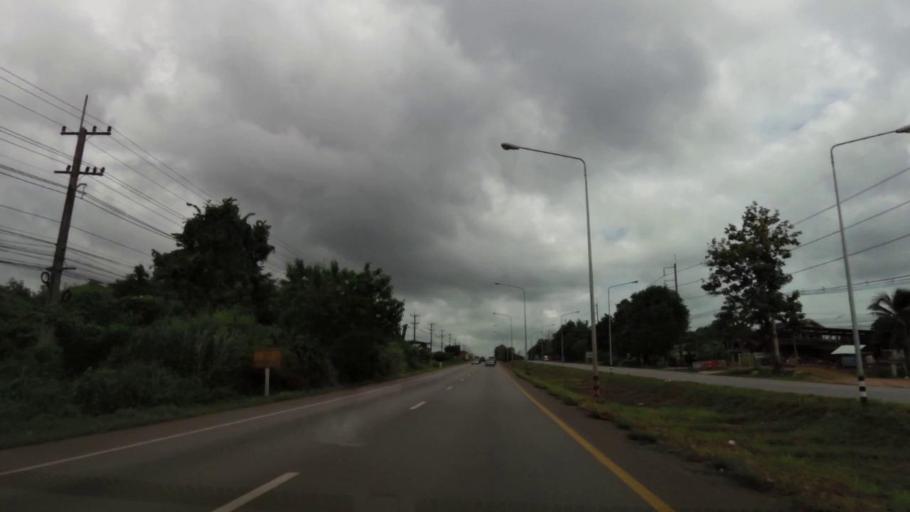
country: TH
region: Chanthaburi
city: Na Yai Am
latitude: 12.7751
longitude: 101.8360
